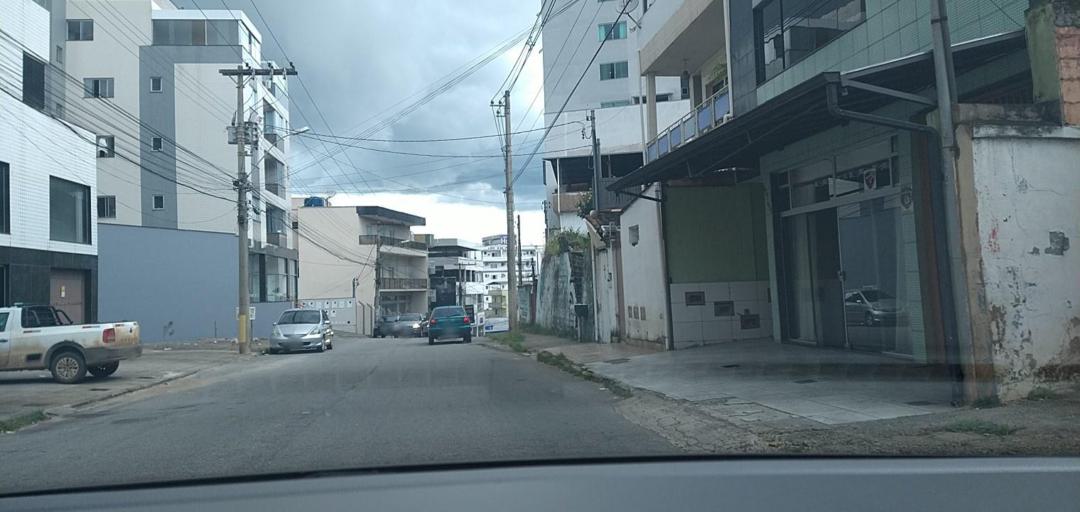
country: BR
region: Minas Gerais
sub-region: Joao Monlevade
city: Joao Monlevade
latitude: -19.8084
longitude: -43.1824
